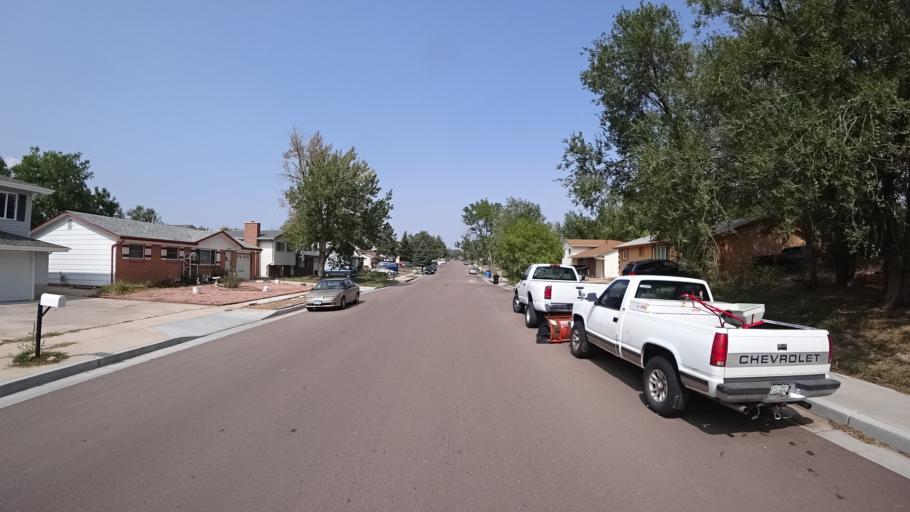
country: US
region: Colorado
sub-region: El Paso County
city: Stratmoor
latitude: 38.8005
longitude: -104.7755
